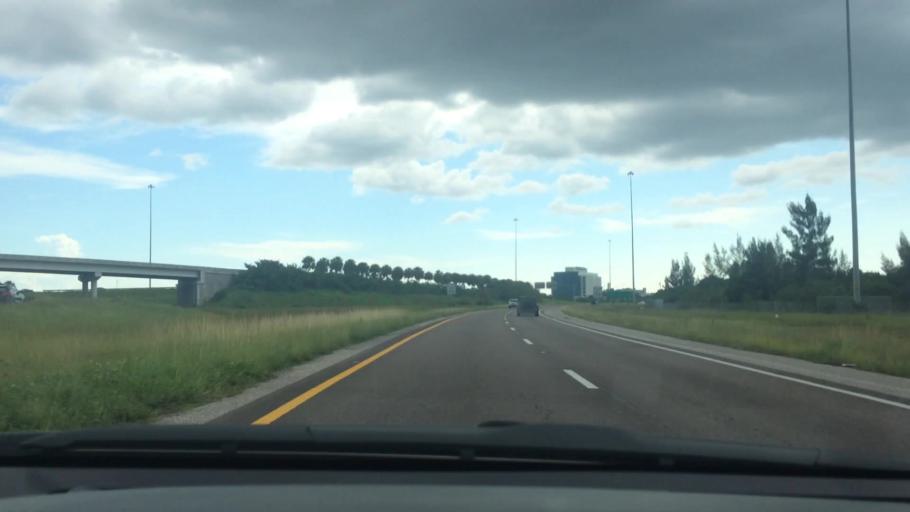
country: US
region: Florida
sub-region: Pinellas County
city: Feather Sound
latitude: 27.8950
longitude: -82.6457
